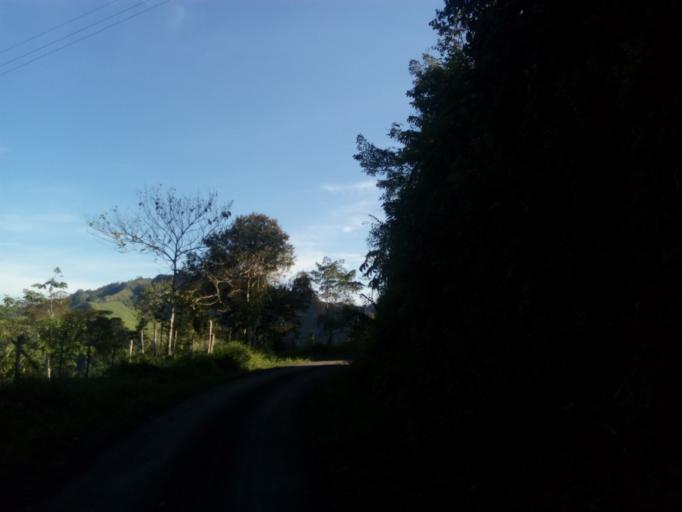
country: CO
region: Boyaca
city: Quipama
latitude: 5.5690
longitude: -74.2005
